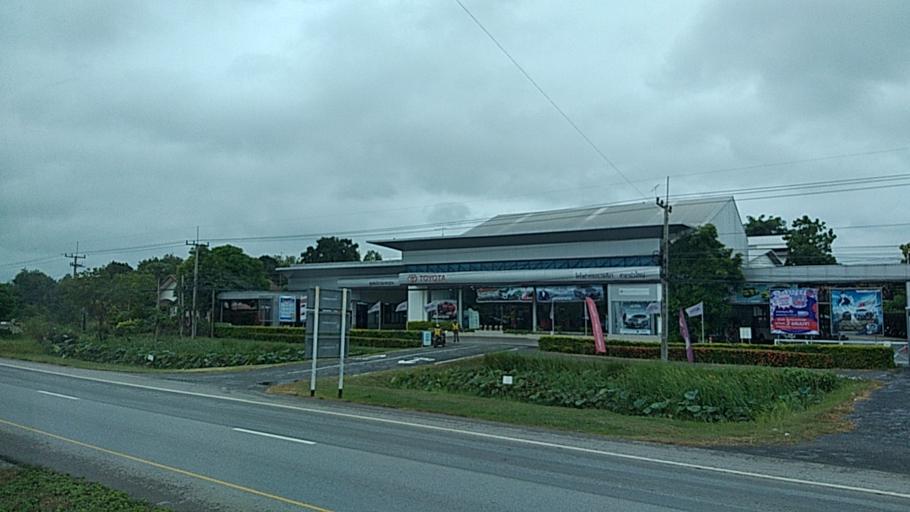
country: TH
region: Nakhon Ratchasima
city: Sida
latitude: 15.5429
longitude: 102.5467
